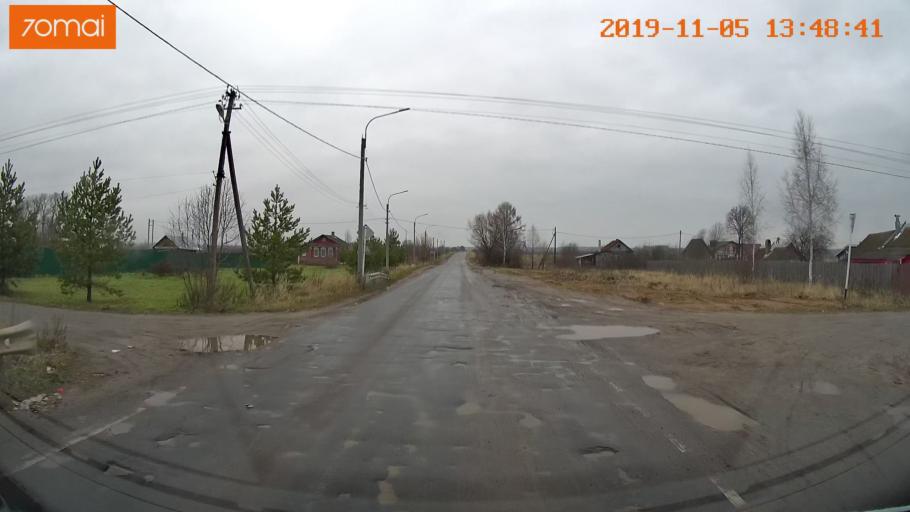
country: RU
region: Ivanovo
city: Shuya
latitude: 57.0047
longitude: 41.4072
